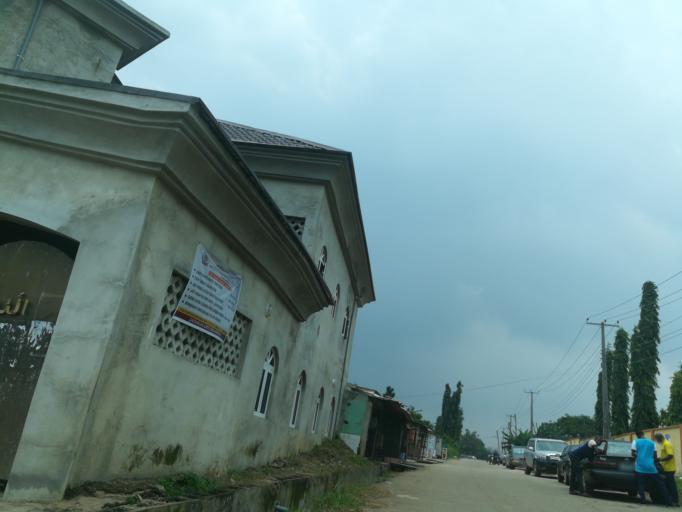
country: NG
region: Lagos
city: Ikorodu
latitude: 6.5642
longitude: 3.5904
